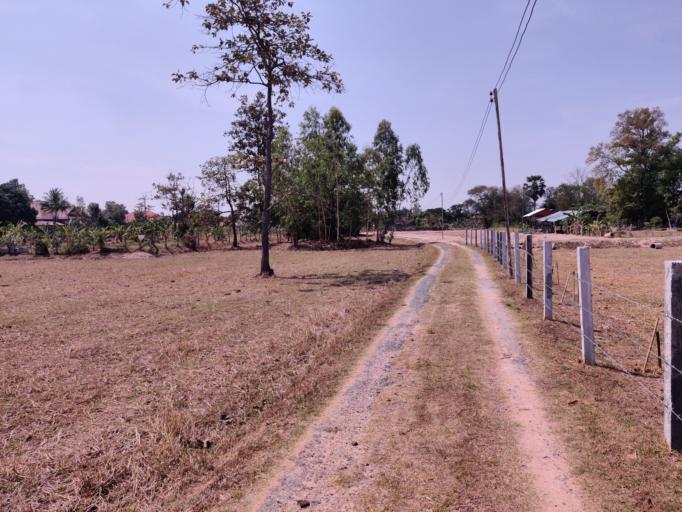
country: TH
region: Sisaket
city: Huai Thap Than
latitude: 15.0524
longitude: 104.0411
